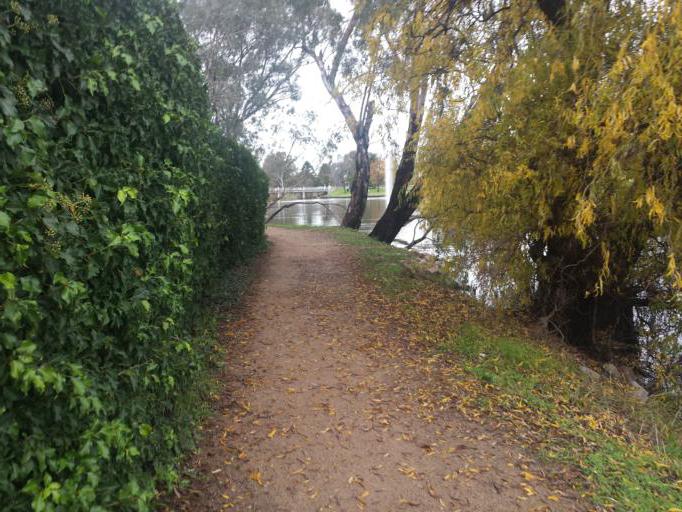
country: AU
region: Victoria
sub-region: Benalla
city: Benalla
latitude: -36.5502
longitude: 145.9791
